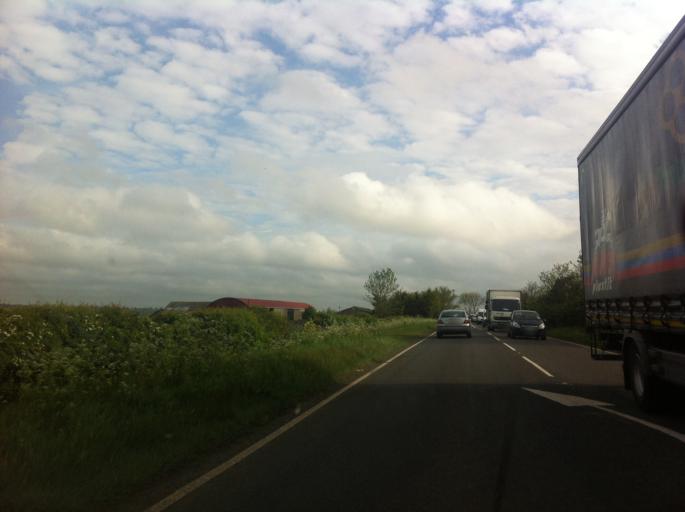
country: GB
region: England
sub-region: Northamptonshire
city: Irchester
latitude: 52.2652
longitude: -0.6778
